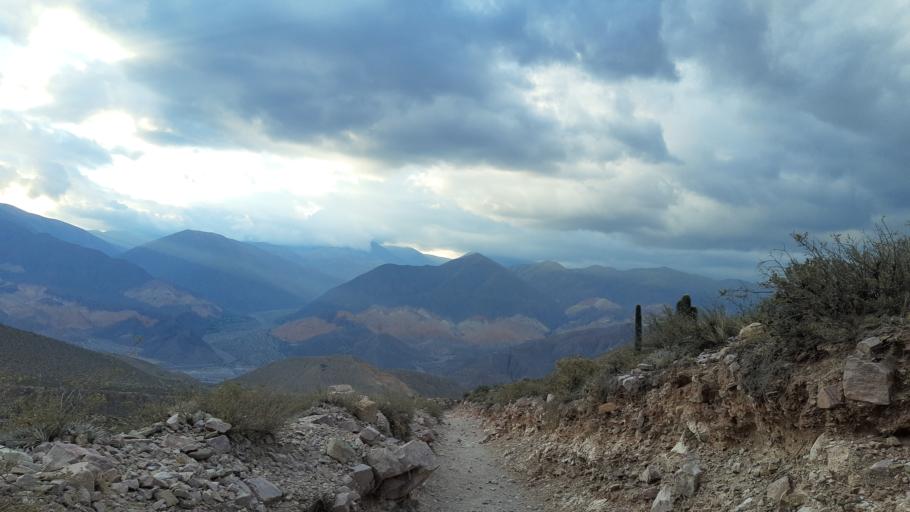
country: AR
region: Jujuy
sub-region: Departamento de Tilcara
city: Tilcara
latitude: -23.5916
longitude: -65.3832
